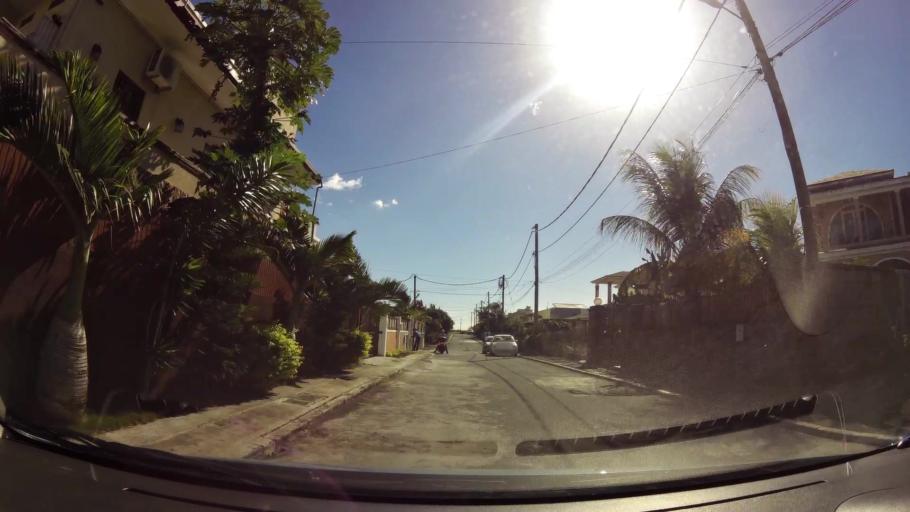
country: MU
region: Black River
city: Flic en Flac
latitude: -20.2785
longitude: 57.3800
